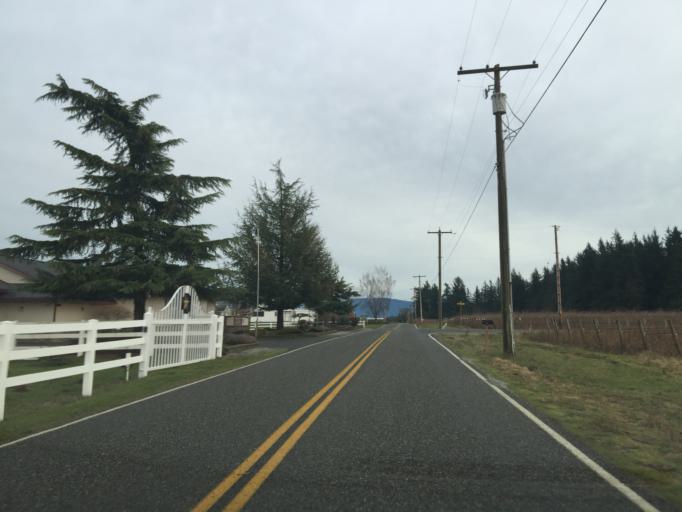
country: US
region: Washington
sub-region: Whatcom County
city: Ferndale
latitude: 48.8988
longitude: -122.5308
